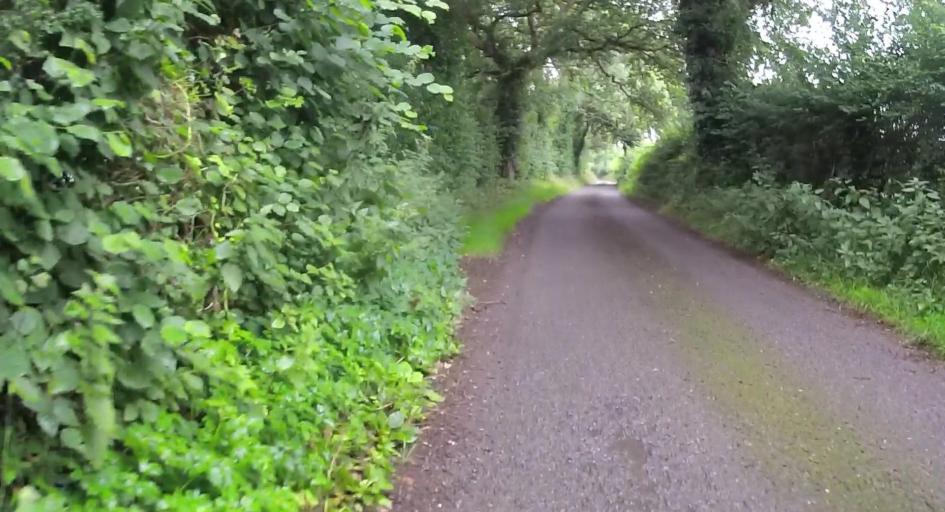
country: GB
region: England
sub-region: Hampshire
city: Highclere
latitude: 51.2731
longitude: -1.3588
